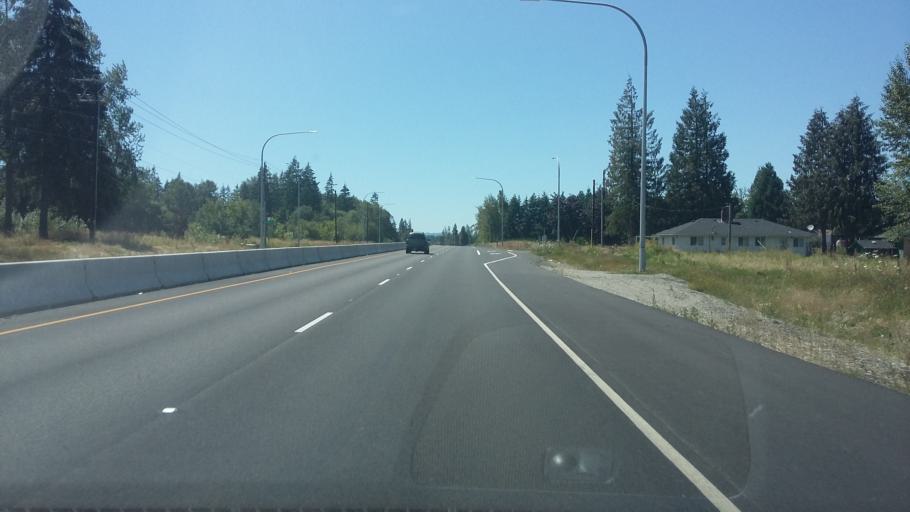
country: US
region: Washington
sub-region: Clark County
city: Dollar Corner
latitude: 45.7798
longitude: -122.6316
